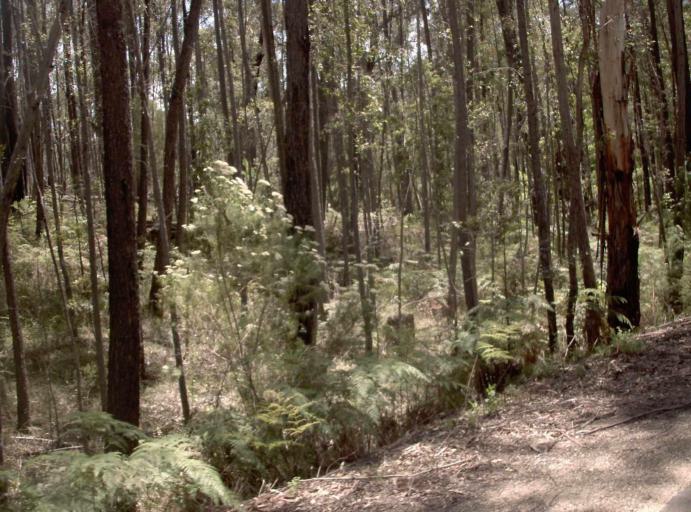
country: AU
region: New South Wales
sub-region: Bombala
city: Bombala
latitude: -37.5797
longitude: 148.9395
